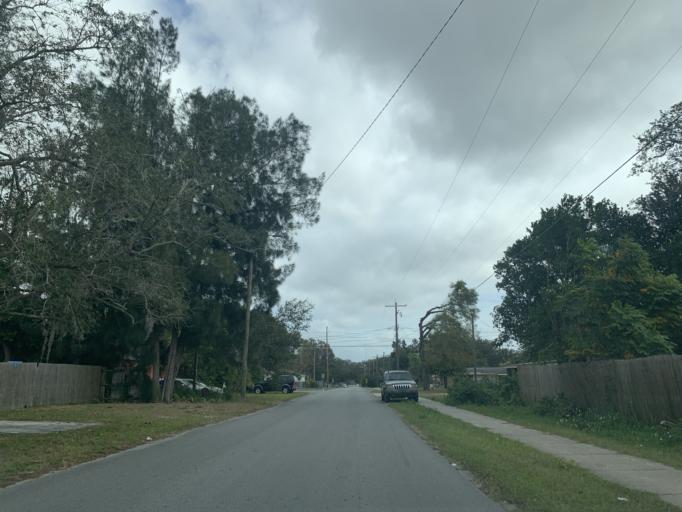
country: US
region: Florida
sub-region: Hillsborough County
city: East Lake-Orient Park
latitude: 27.9796
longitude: -82.3952
